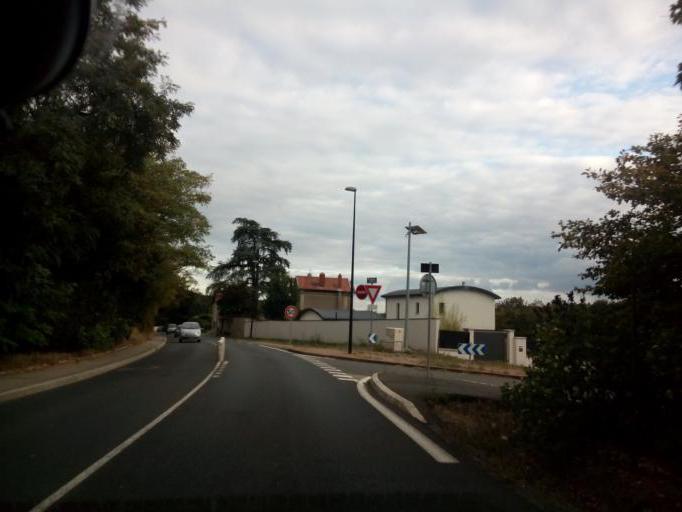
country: FR
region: Rhone-Alpes
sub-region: Departement du Rhone
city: Sainte-Consorce
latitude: 45.7824
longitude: 4.7203
